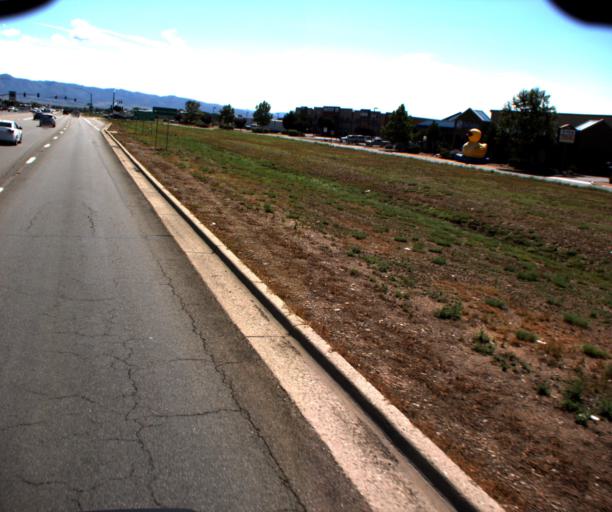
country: US
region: Arizona
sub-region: Yavapai County
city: Prescott Valley
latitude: 34.5825
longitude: -112.3452
